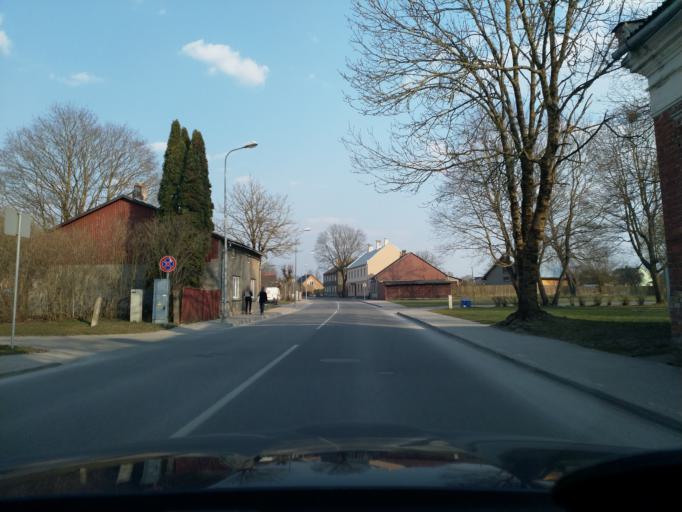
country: LV
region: Grobina
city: Grobina
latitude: 56.5352
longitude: 21.1722
